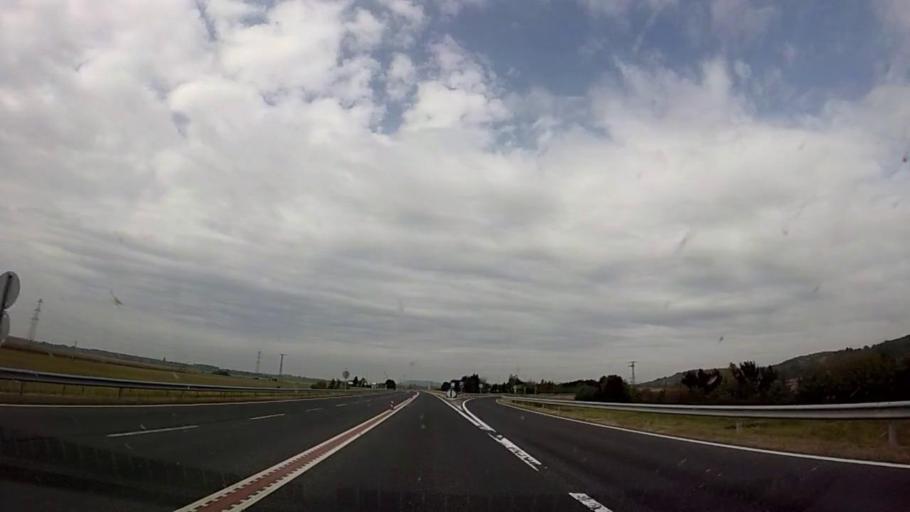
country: HR
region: Medimurska
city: Domasinec
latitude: 46.5021
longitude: 16.6123
